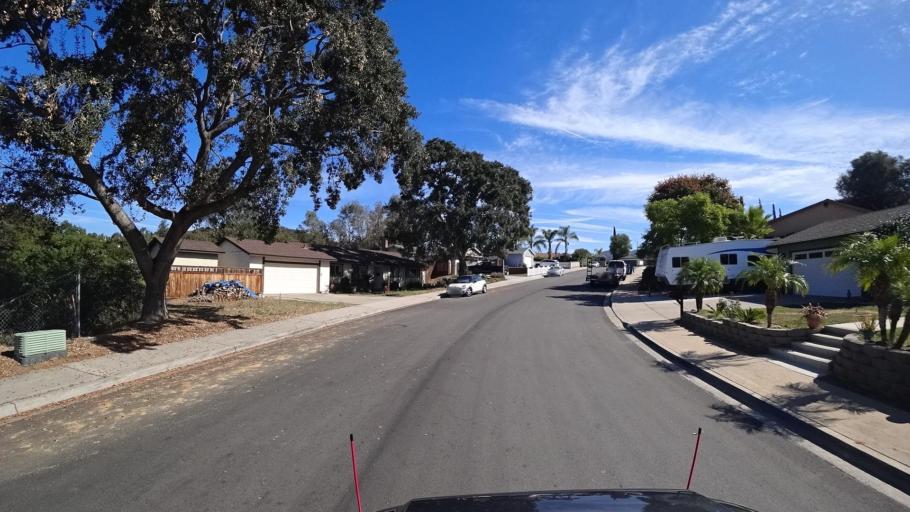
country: US
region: California
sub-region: San Diego County
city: Lakeside
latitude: 32.8420
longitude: -116.9033
